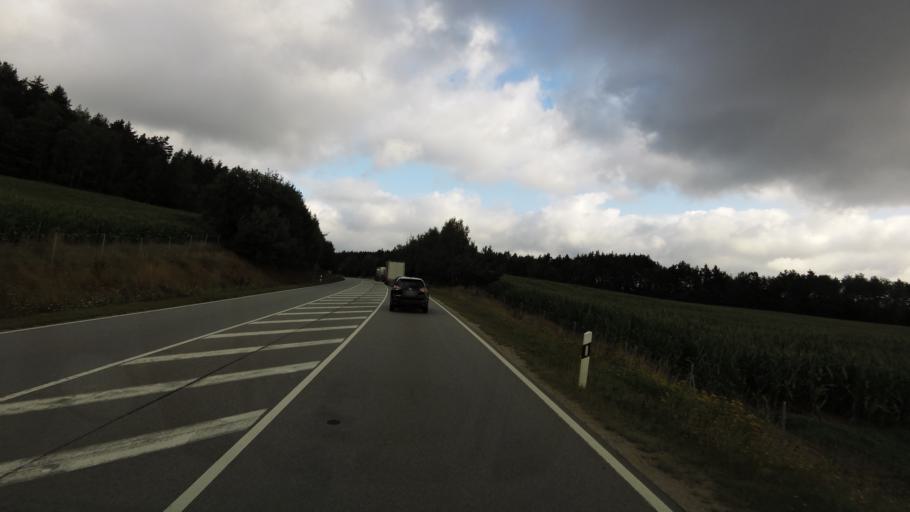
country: DE
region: Bavaria
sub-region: Upper Palatinate
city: Traitsching
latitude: 49.1696
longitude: 12.6565
